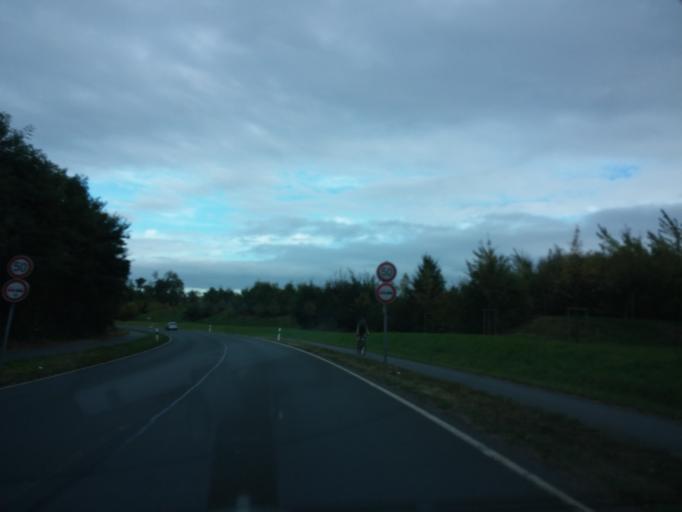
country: DE
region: North Rhine-Westphalia
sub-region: Regierungsbezirk Munster
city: Gelsenkirchen
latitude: 51.5234
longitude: 7.1407
